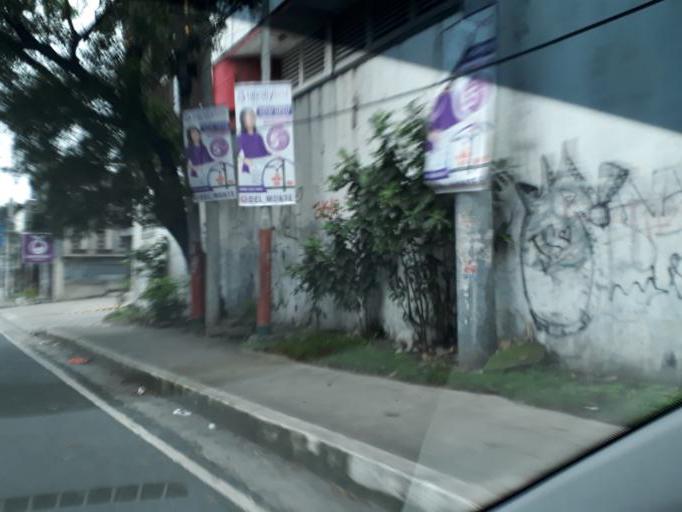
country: PH
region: Calabarzon
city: Del Monte
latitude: 14.6396
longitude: 121.0092
